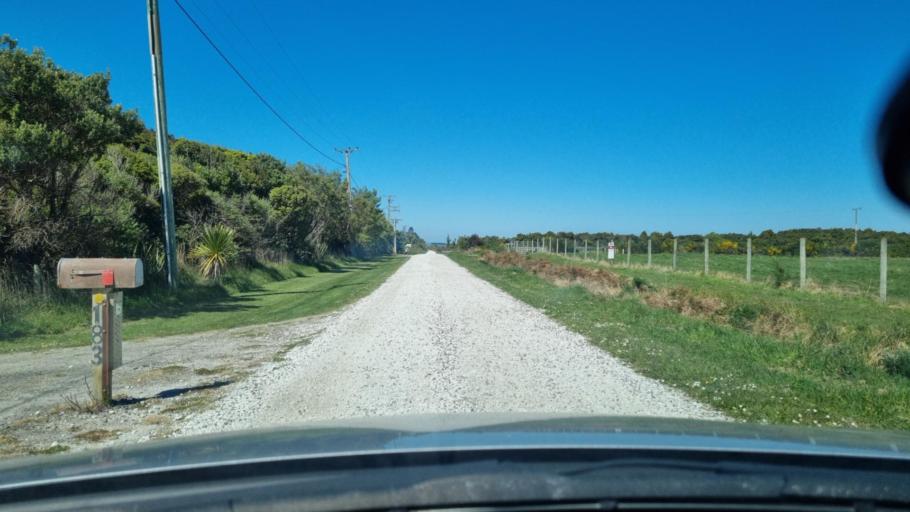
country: NZ
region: Southland
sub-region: Invercargill City
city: Invercargill
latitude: -46.4497
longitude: 168.3166
